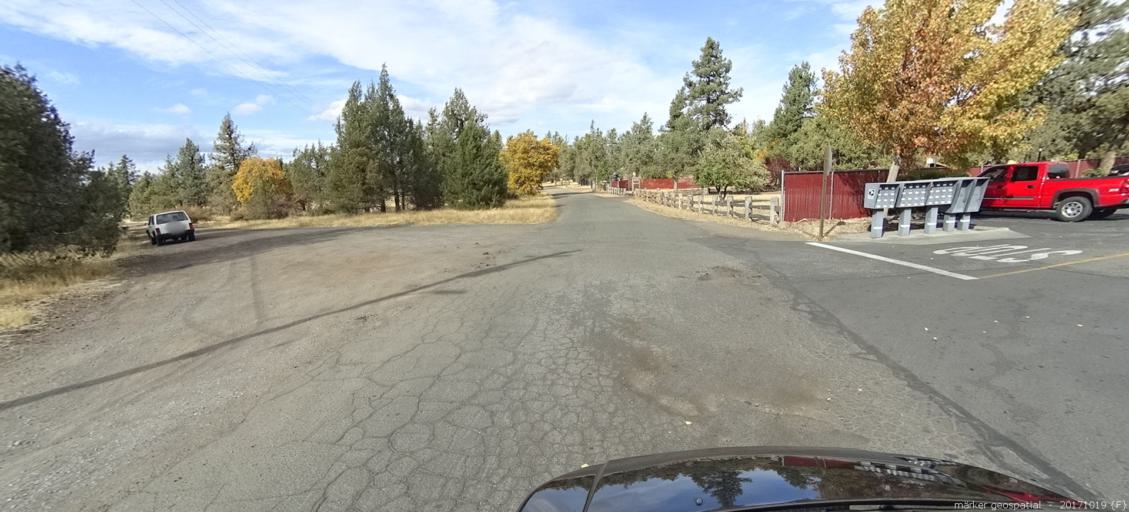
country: US
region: California
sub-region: Shasta County
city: Burney
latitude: 41.0029
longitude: -121.4465
